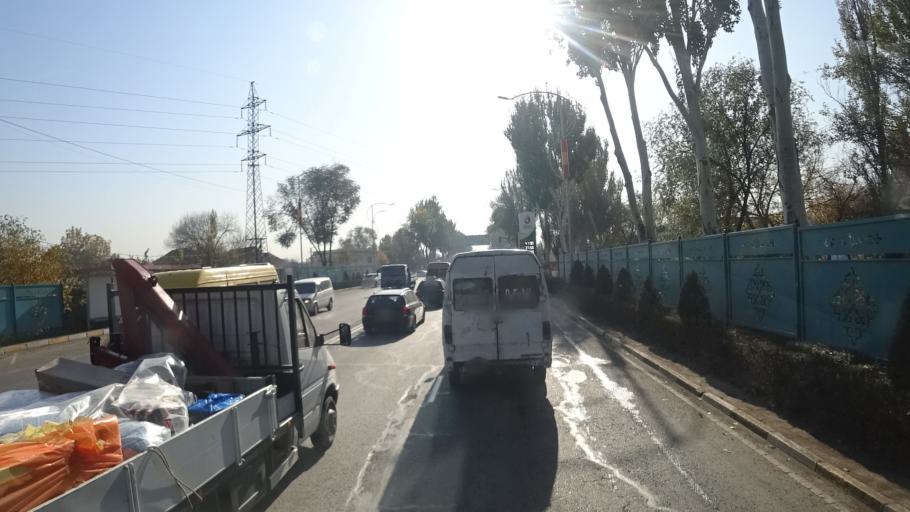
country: KG
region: Chuy
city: Bishkek
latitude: 42.8882
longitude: 74.5502
